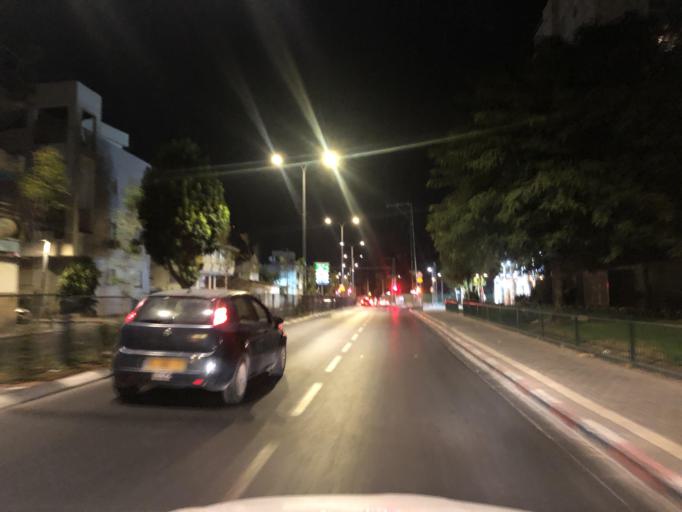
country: IL
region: Tel Aviv
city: Azor
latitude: 32.0473
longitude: 34.7906
